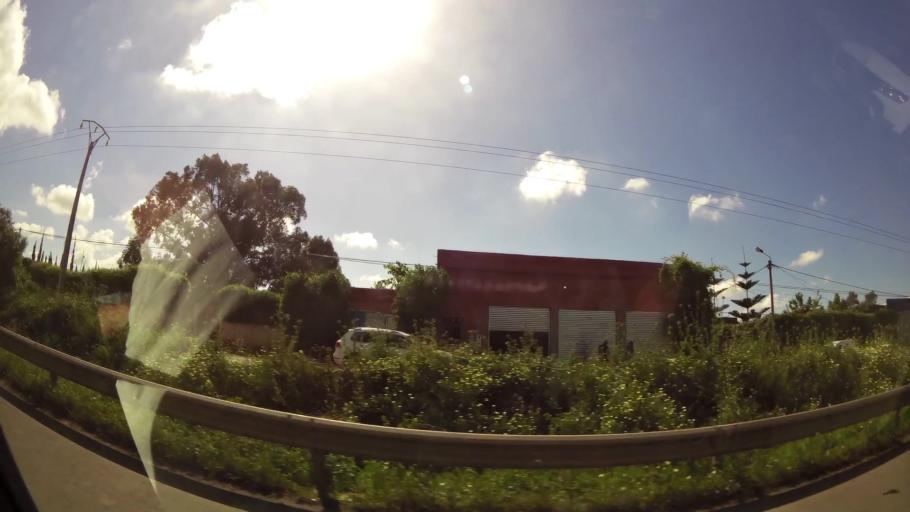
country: MA
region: Grand Casablanca
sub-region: Nouaceur
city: Bouskoura
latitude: 33.4658
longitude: -7.6335
